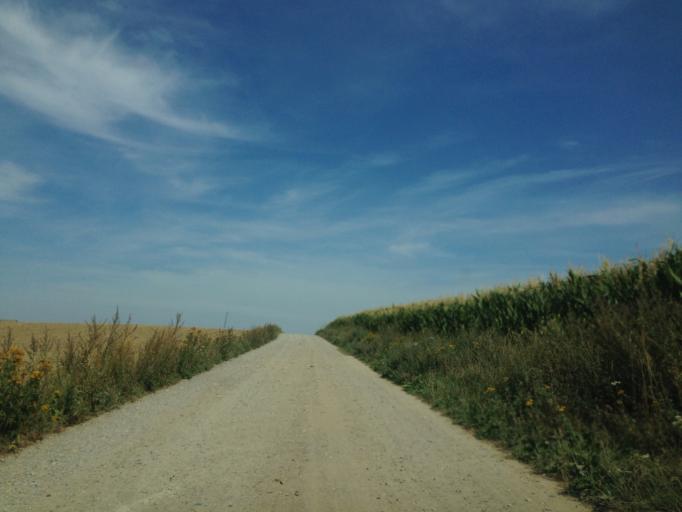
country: PL
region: Kujawsko-Pomorskie
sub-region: Powiat brodnicki
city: Swiedziebnia
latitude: 53.2193
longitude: 19.5360
